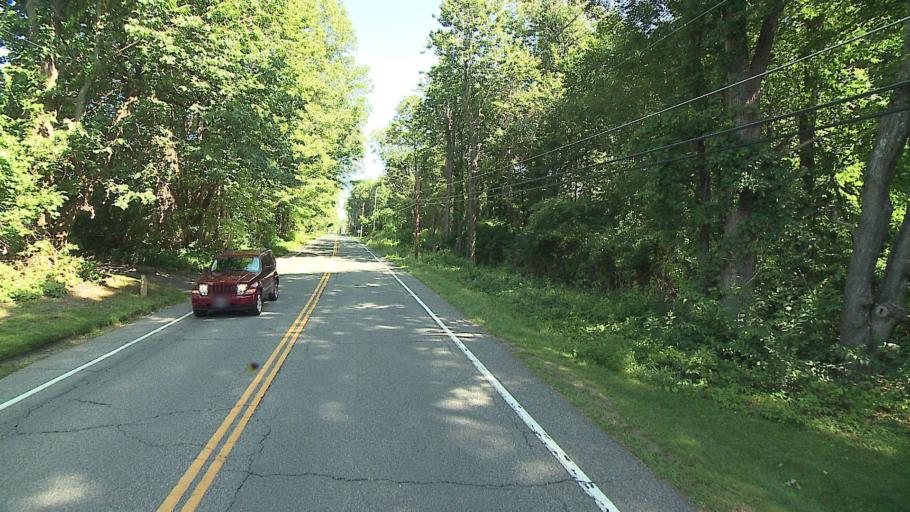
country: US
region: Connecticut
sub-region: Litchfield County
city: Canaan
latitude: 42.0028
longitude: -73.4239
